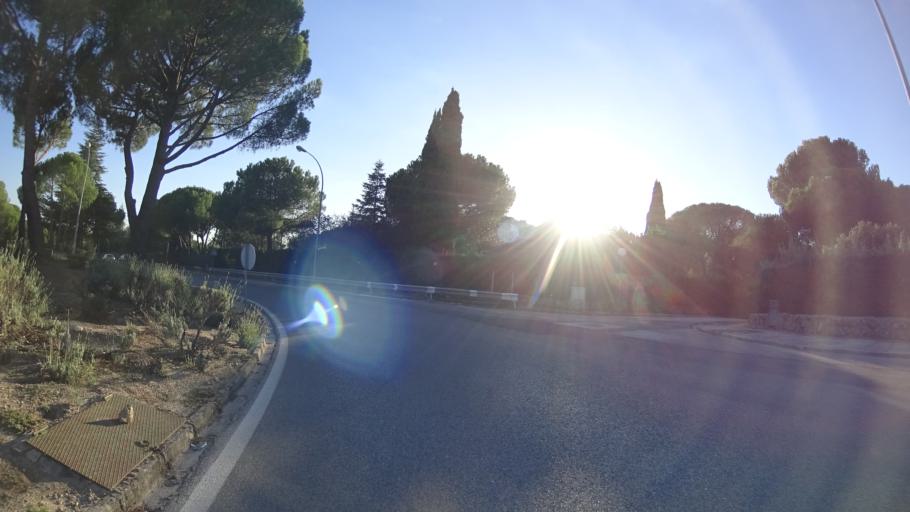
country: ES
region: Madrid
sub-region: Provincia de Madrid
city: Torrelodones
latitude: 40.6008
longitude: -3.9473
